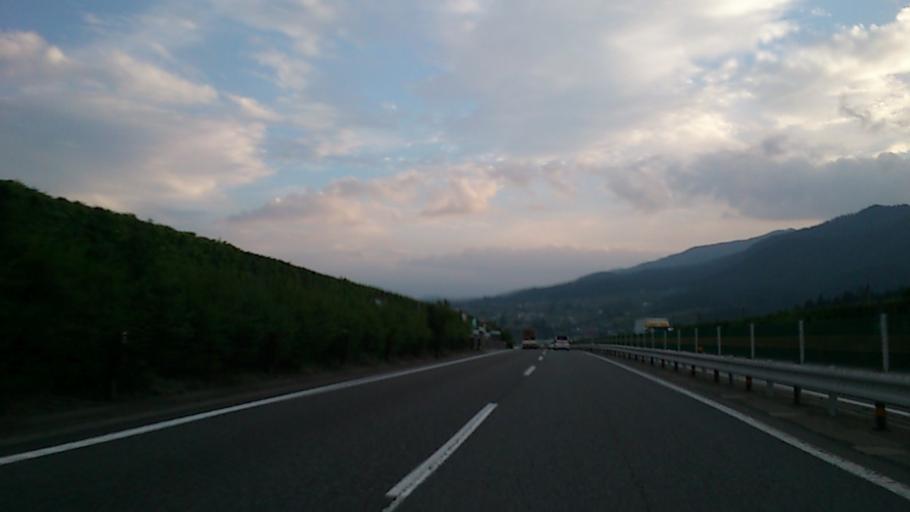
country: JP
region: Nagano
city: Iida
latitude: 35.5212
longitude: 137.8092
